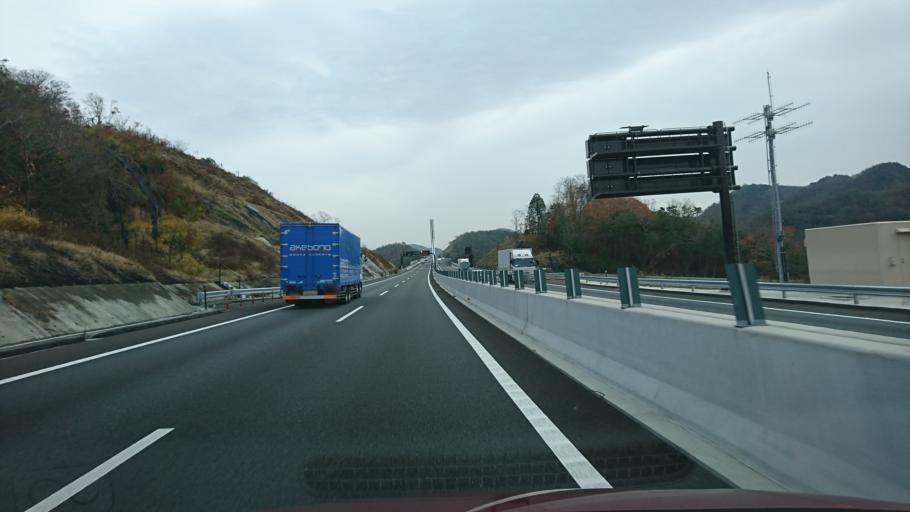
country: JP
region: Hyogo
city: Sandacho
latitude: 34.8649
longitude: 135.2699
